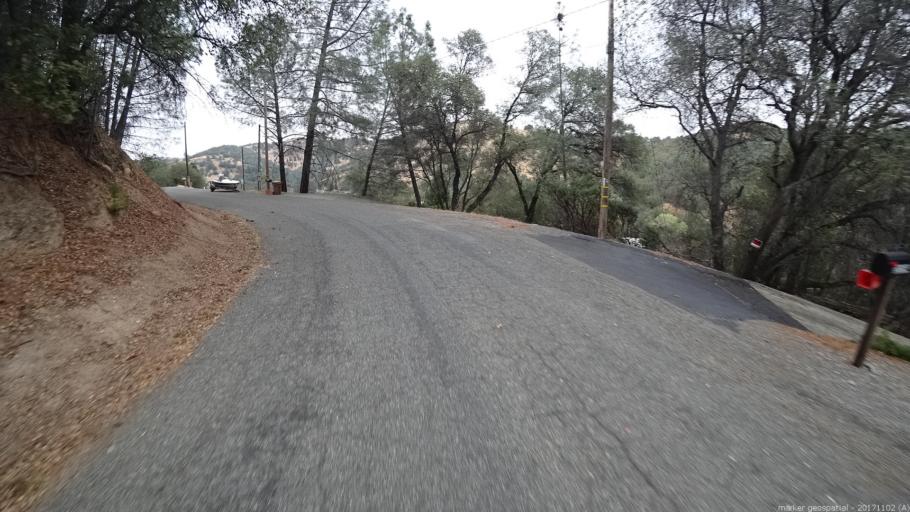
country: US
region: California
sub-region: Shasta County
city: Bella Vista
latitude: 40.7156
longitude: -122.2371
